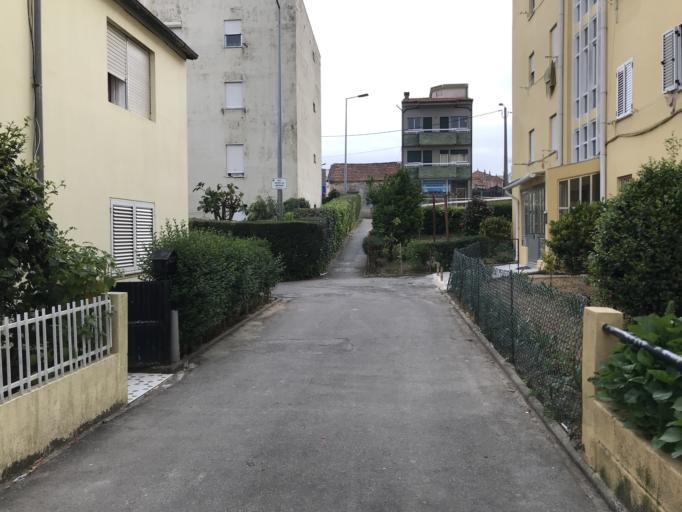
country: PT
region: Porto
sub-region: Matosinhos
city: Matosinhos
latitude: 41.1819
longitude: -8.6714
